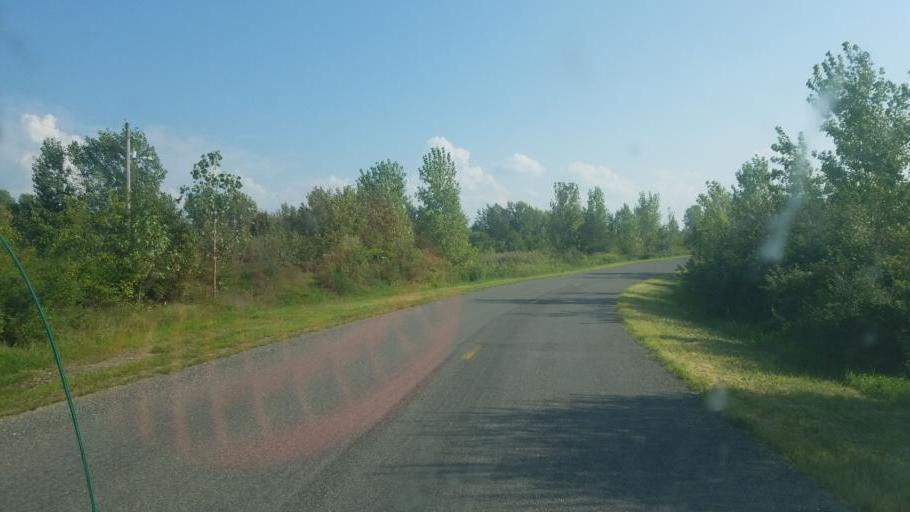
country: US
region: Ohio
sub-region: Medina County
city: Westfield Center
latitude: 41.0071
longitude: -81.9604
